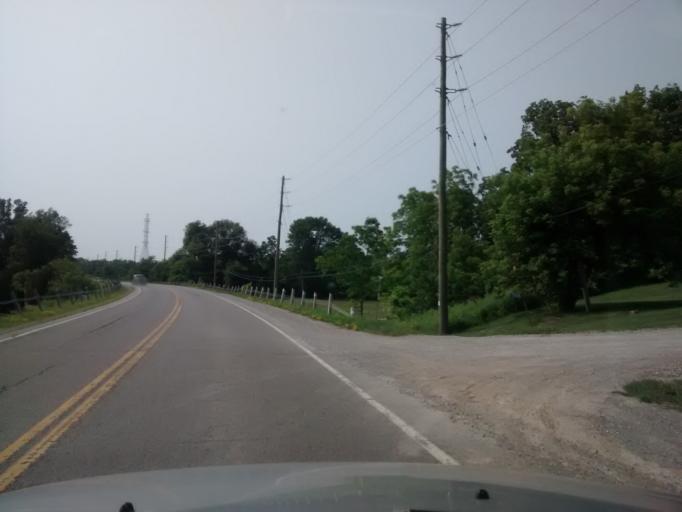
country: CA
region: Ontario
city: Ancaster
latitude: 43.0589
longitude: -79.9157
